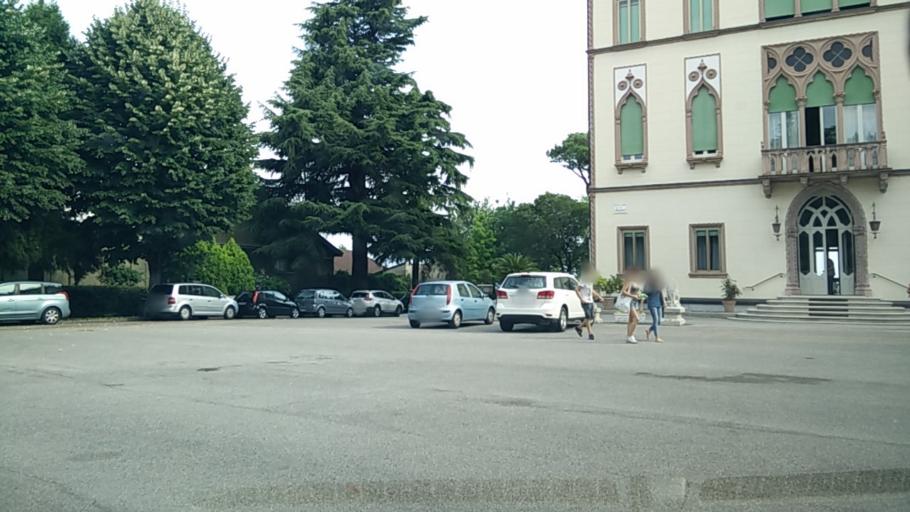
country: IT
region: Lombardy
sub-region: Provincia di Brescia
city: Desenzano del Garda
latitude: 45.4636
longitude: 10.5565
